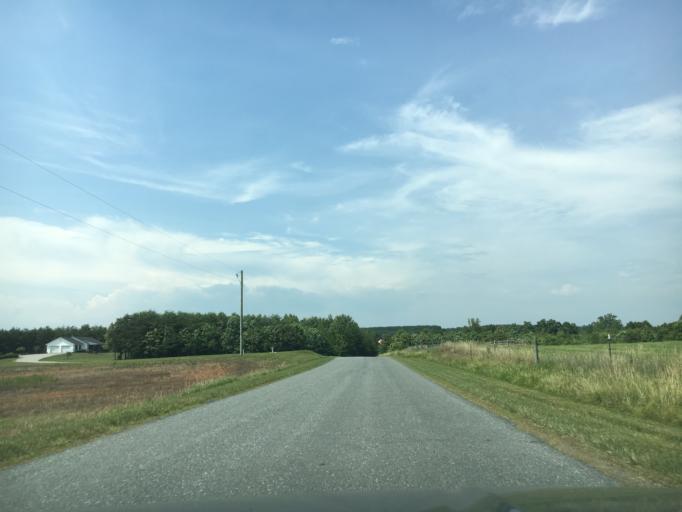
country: US
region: Virginia
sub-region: Pittsylvania County
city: Gretna
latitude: 36.9393
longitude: -79.4416
